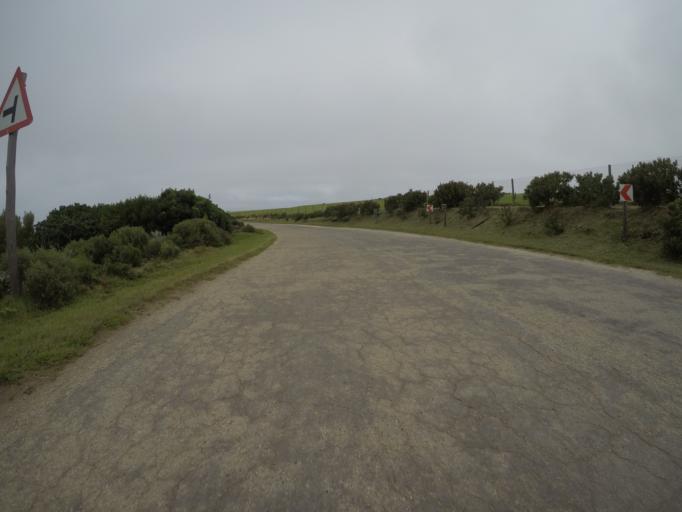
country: ZA
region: Eastern Cape
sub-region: Cacadu District Municipality
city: Kareedouw
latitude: -34.0715
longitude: 24.2329
